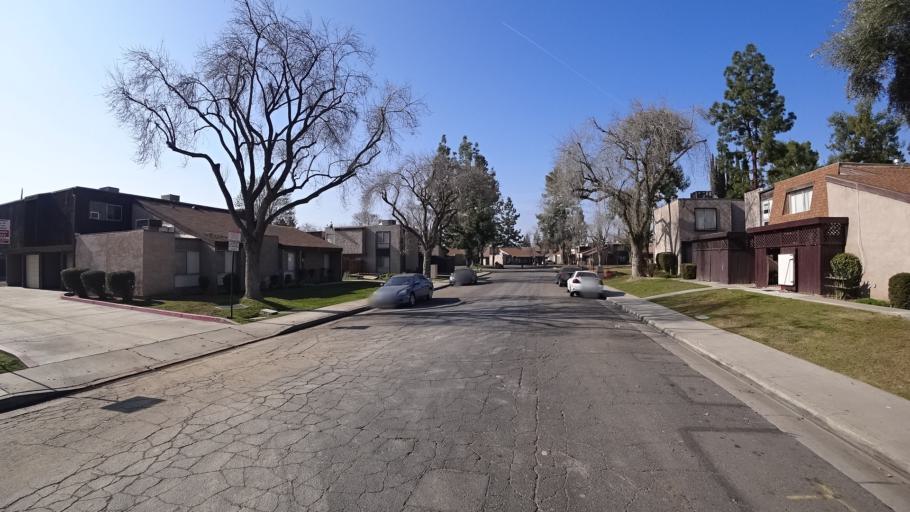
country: US
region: California
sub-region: Kern County
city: Bakersfield
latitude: 35.3346
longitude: -119.0687
